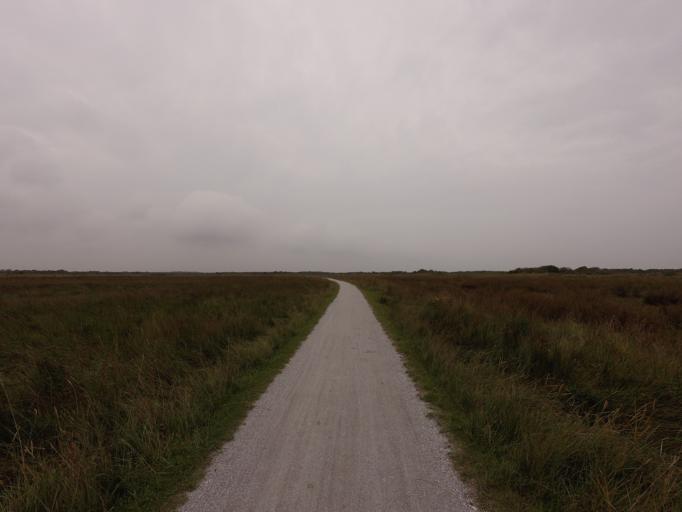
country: NL
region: Friesland
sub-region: Gemeente Schiermonnikoog
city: Schiermonnikoog
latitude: 53.4879
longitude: 6.2090
